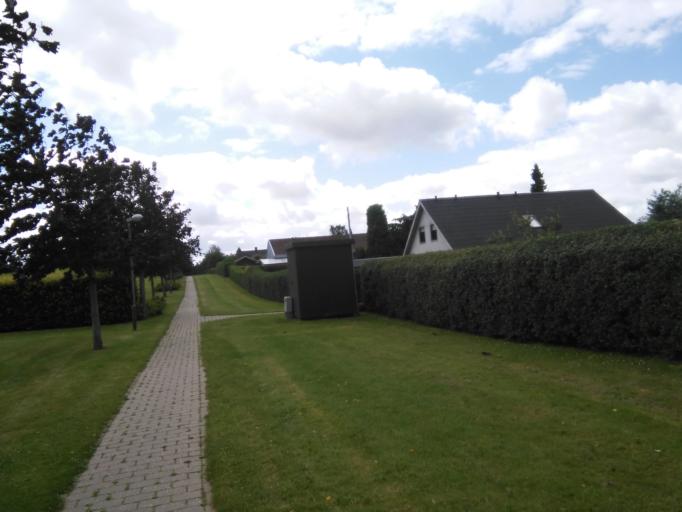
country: DK
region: Central Jutland
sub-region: Arhus Kommune
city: Marslet
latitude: 56.0747
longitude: 10.1533
